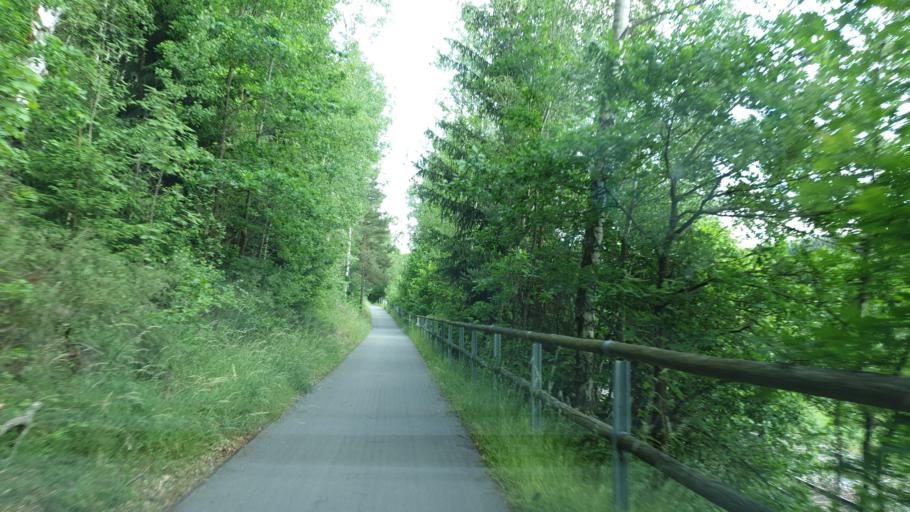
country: DE
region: Saxony
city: Adorf
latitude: 50.3427
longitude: 12.2485
